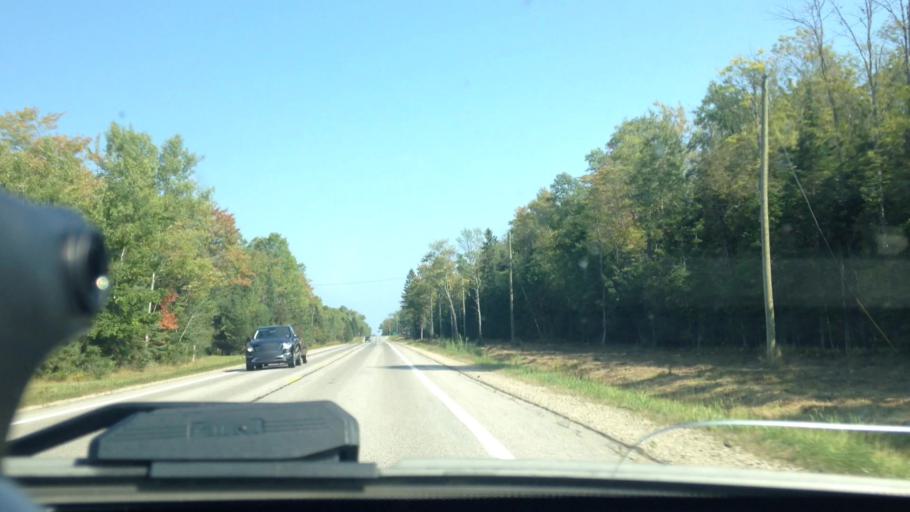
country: US
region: Michigan
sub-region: Luce County
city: Newberry
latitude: 46.3034
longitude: -85.3717
